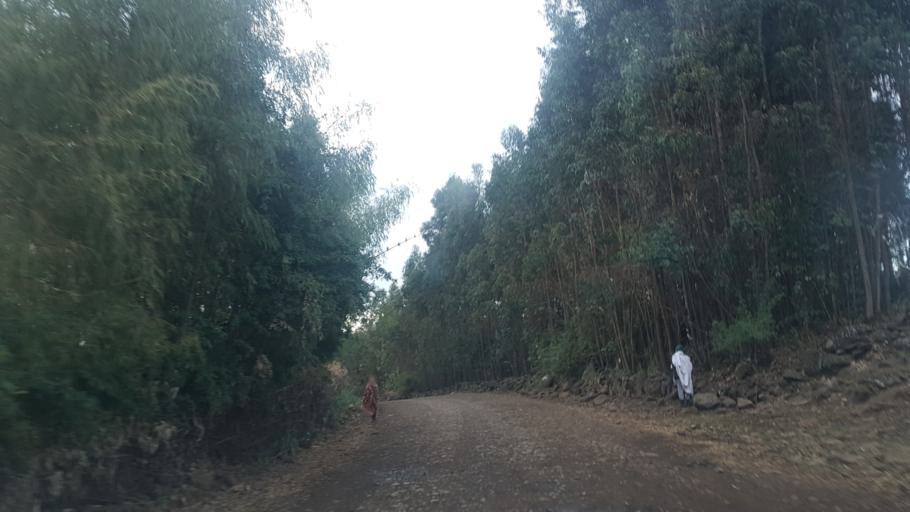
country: ET
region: Amhara
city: Finote Selam
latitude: 10.8188
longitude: 37.6419
